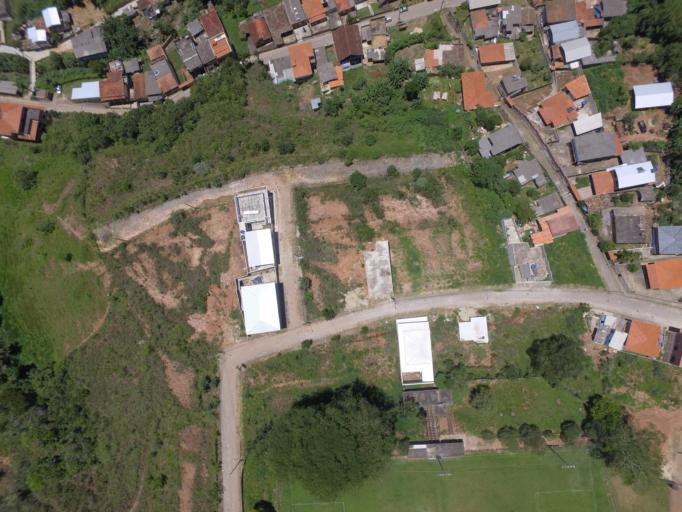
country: BR
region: Minas Gerais
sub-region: Tiradentes
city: Tiradentes
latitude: -21.0633
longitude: -44.0794
